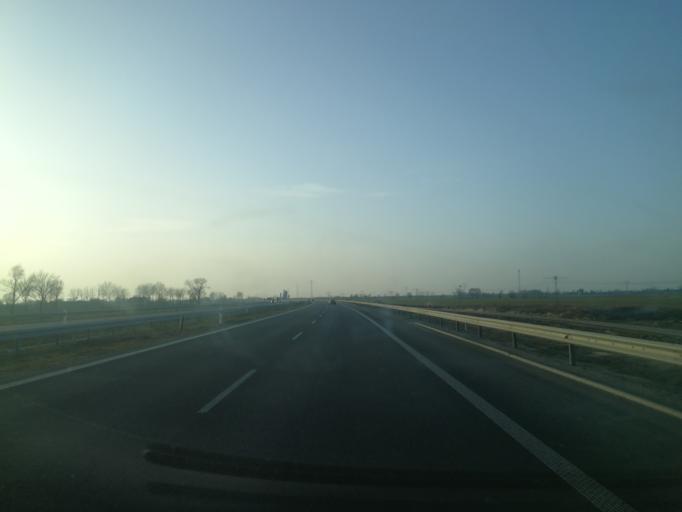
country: PL
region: Pomeranian Voivodeship
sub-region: Powiat nowodworski
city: Ostaszewo
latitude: 54.2521
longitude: 18.9796
